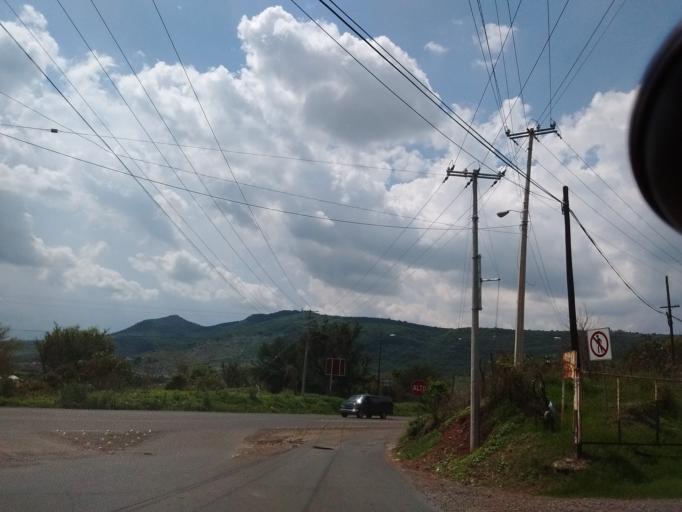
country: MX
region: Jalisco
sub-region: Atotonilco el Alto
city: Vistas del Maguey [Fraccionamiento]
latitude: 20.5331
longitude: -102.5213
